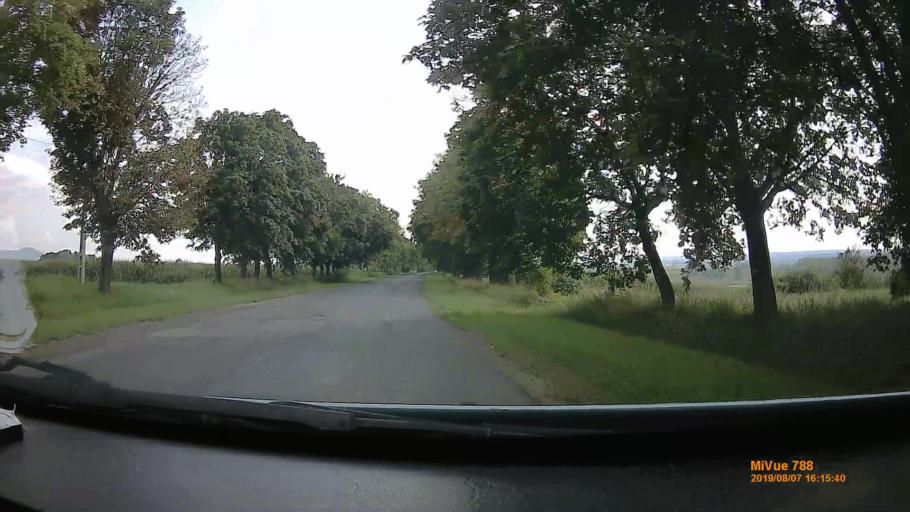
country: HU
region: Borsod-Abauj-Zemplen
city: Gonc
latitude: 48.4680
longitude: 21.2540
